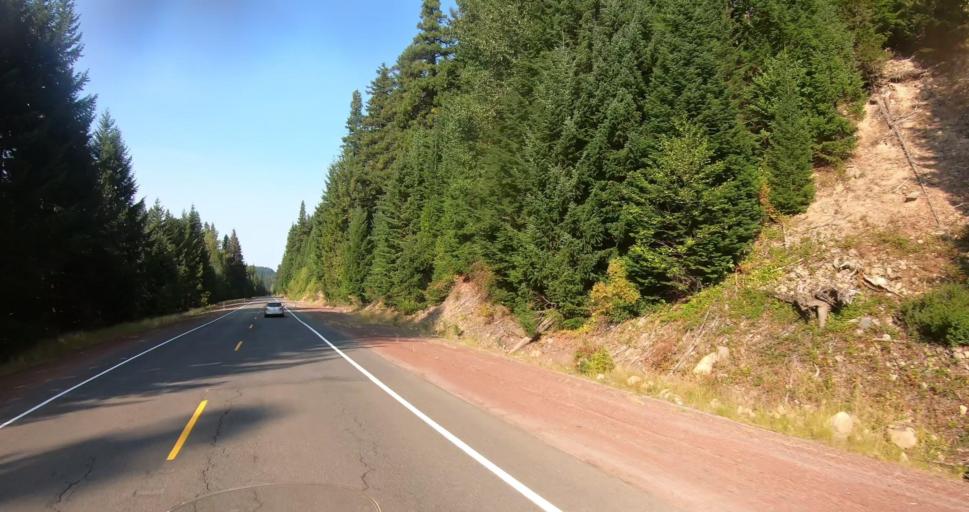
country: US
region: Oregon
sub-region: Hood River County
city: Odell
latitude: 45.3795
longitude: -121.5672
